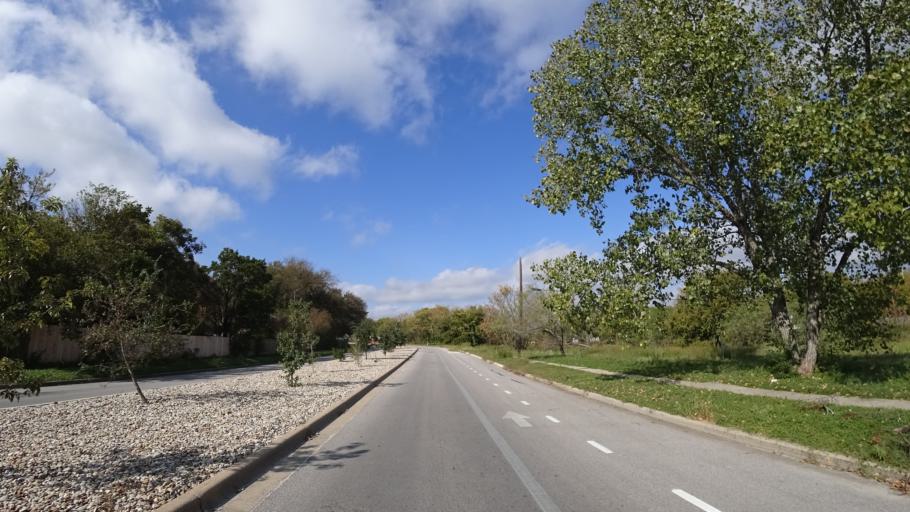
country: US
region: Texas
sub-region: Travis County
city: Shady Hollow
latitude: 30.1910
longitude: -97.8270
